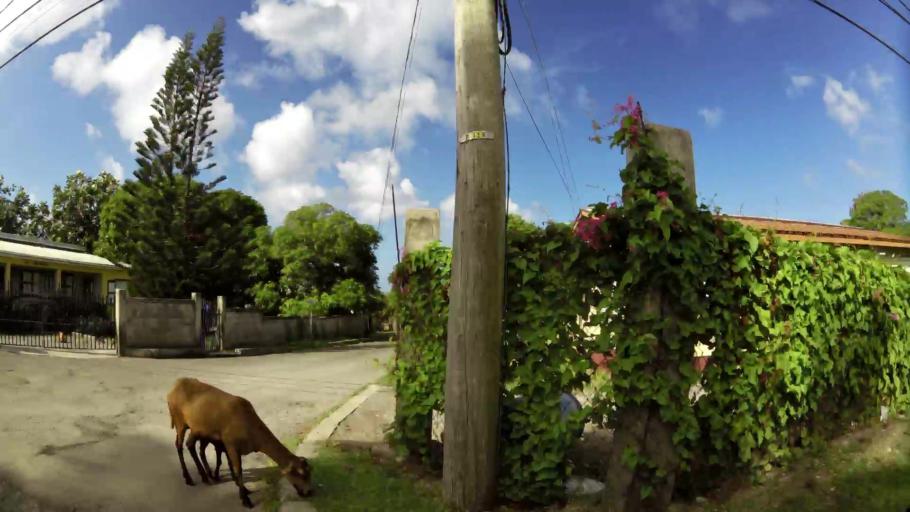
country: KN
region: Saint Paul Charlestown
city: Charlestown
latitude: 17.1343
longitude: -62.6186
